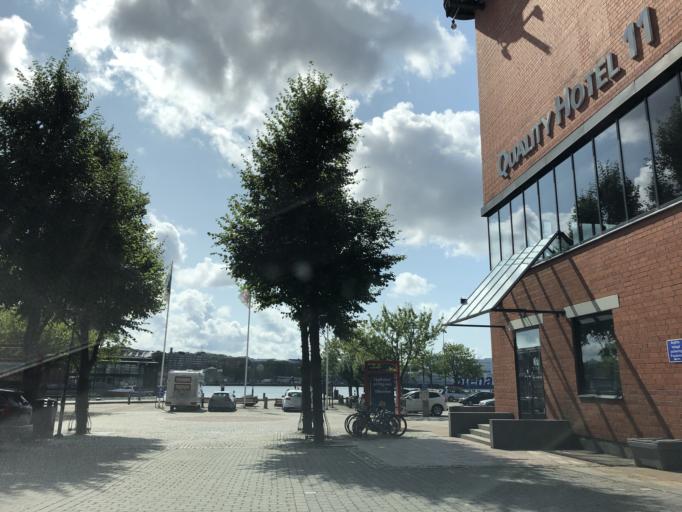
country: SE
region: Vaestra Goetaland
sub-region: Goteborg
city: Majorna
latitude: 57.7011
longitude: 11.9139
